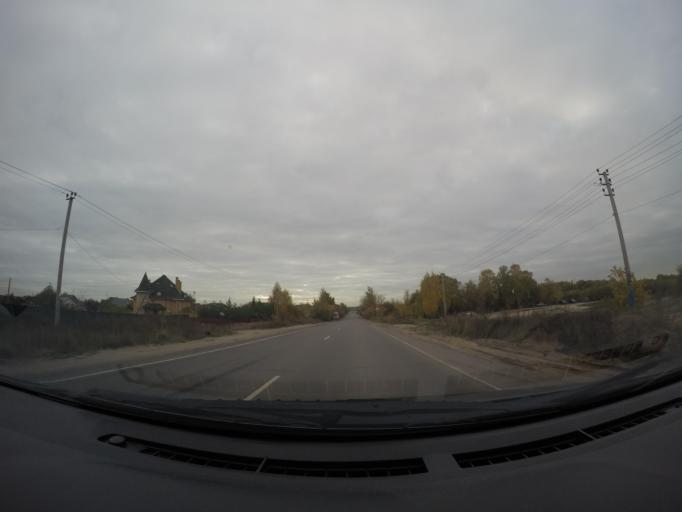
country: RU
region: Moskovskaya
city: Staraya Kupavna
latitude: 55.7751
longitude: 38.1938
